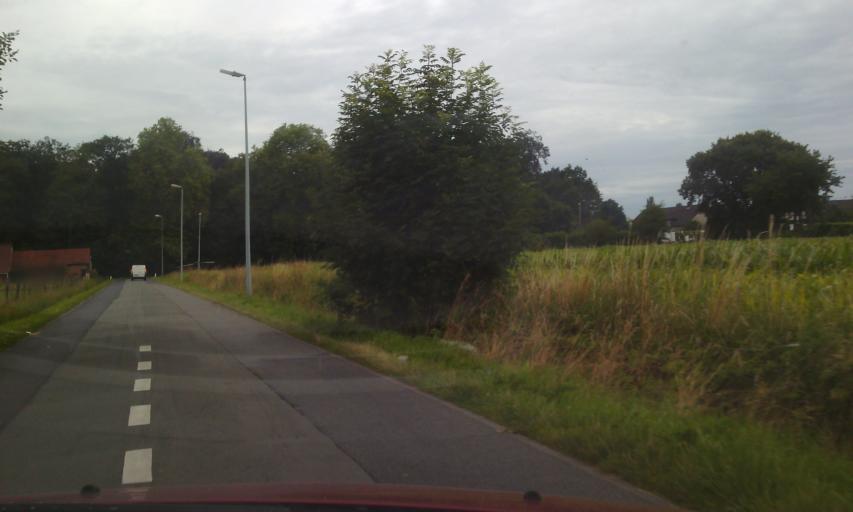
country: BE
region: Flanders
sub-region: Provincie Oost-Vlaanderen
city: Zele
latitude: 51.0798
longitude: 4.0362
